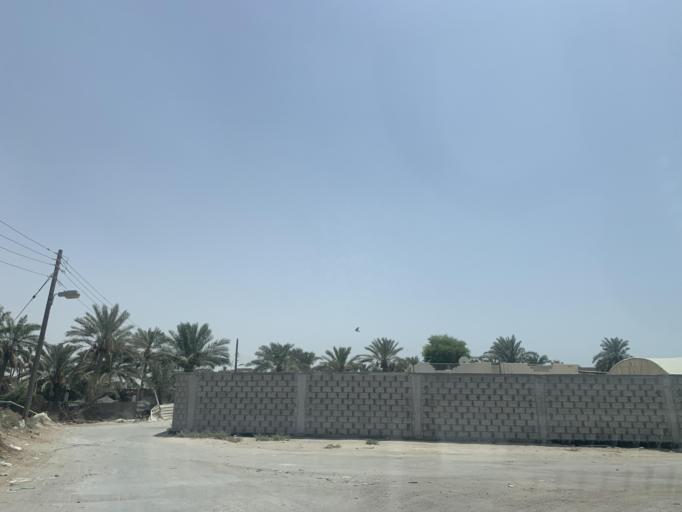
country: BH
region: Central Governorate
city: Madinat Hamad
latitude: 26.1544
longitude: 50.4968
